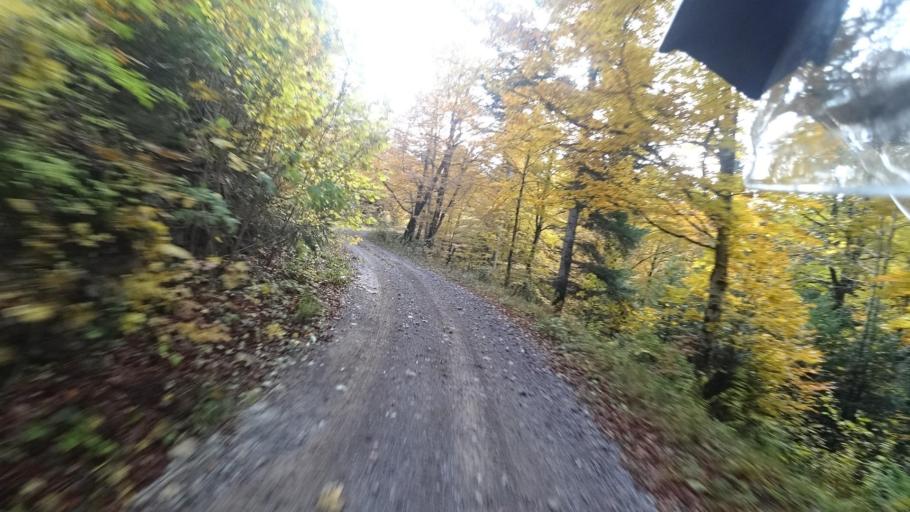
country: HR
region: Karlovacka
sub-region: Grad Ogulin
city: Ogulin
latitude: 45.2058
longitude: 15.1027
